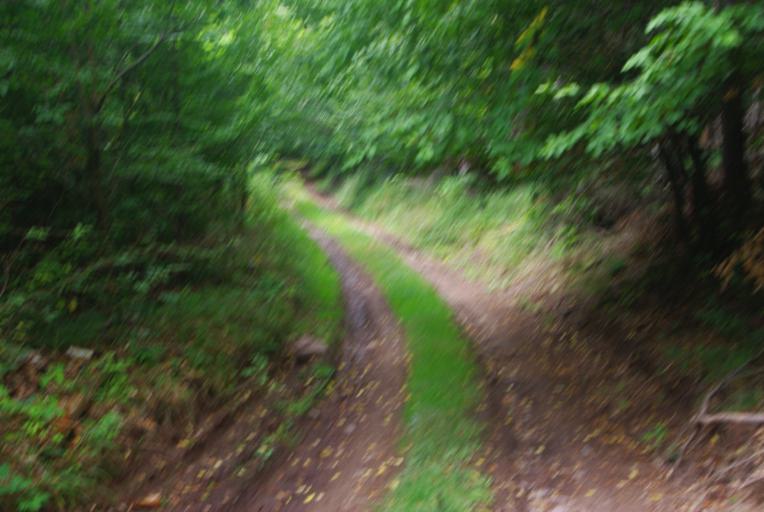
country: HU
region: Borsod-Abauj-Zemplen
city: Gonc
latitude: 48.4106
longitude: 21.3758
